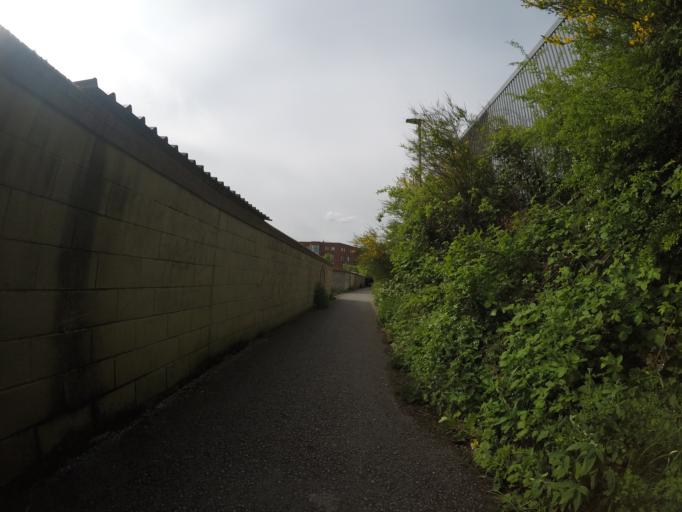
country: GB
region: England
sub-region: City of York
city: York
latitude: 53.9609
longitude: -1.0682
